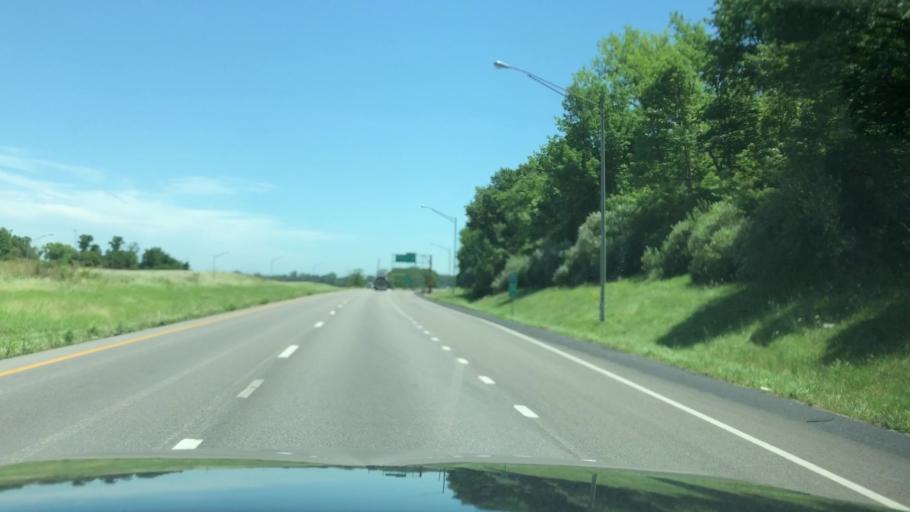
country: US
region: Missouri
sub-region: Saint Louis County
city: Glasgow Village
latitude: 38.7675
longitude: -90.1885
